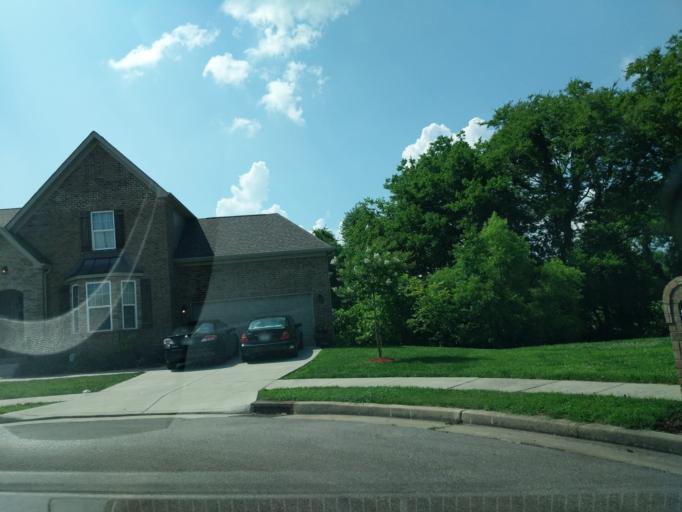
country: US
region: Tennessee
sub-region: Davidson County
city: Goodlettsville
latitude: 36.2807
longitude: -86.6798
